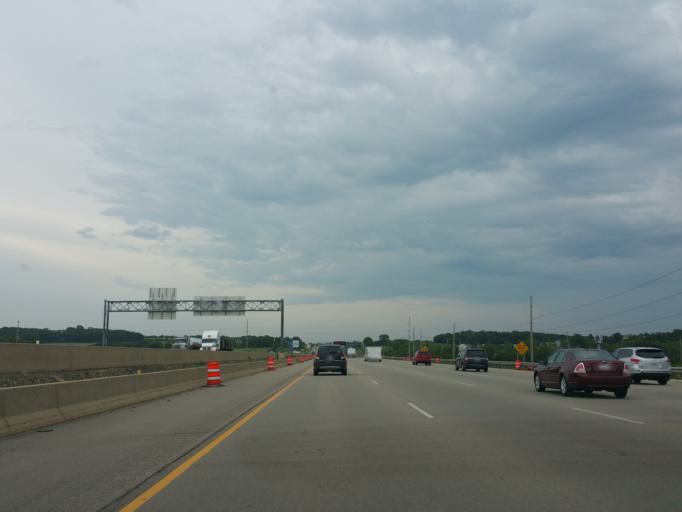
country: US
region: Wisconsin
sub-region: Dane County
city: Monona
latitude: 43.1280
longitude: -89.2918
